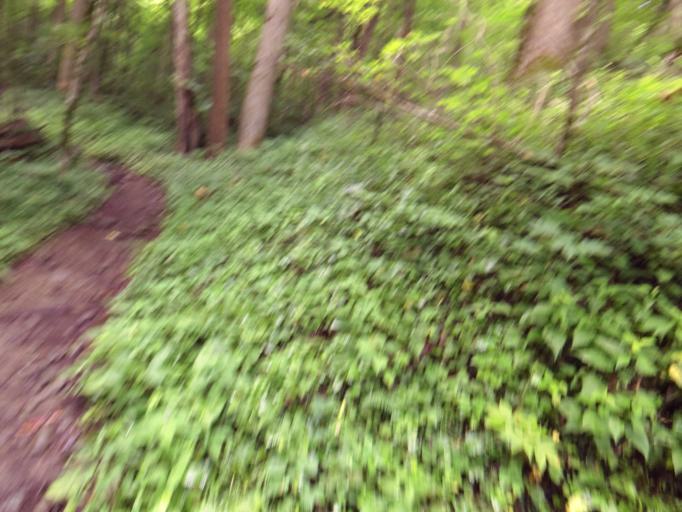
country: US
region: Tennessee
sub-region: Blount County
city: Wildwood
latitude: 35.5870
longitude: -83.7529
